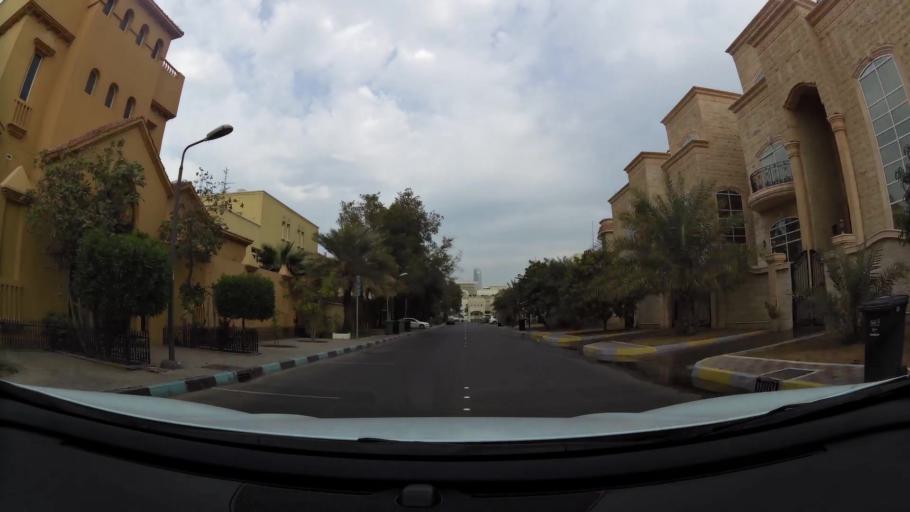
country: AE
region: Abu Dhabi
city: Abu Dhabi
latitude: 24.4651
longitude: 54.3685
